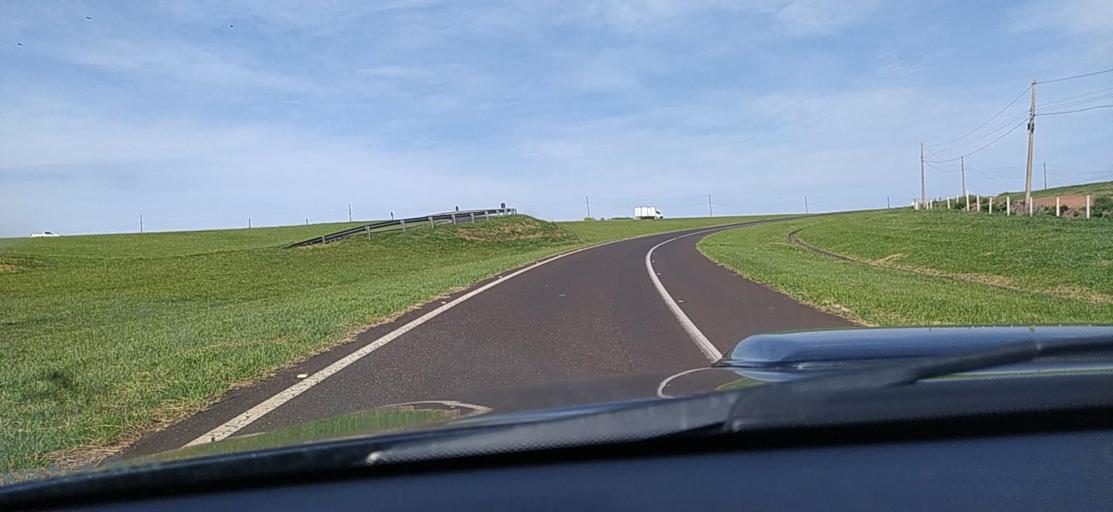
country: BR
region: Sao Paulo
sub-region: Pindorama
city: Pindorama
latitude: -21.2068
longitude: -48.9316
